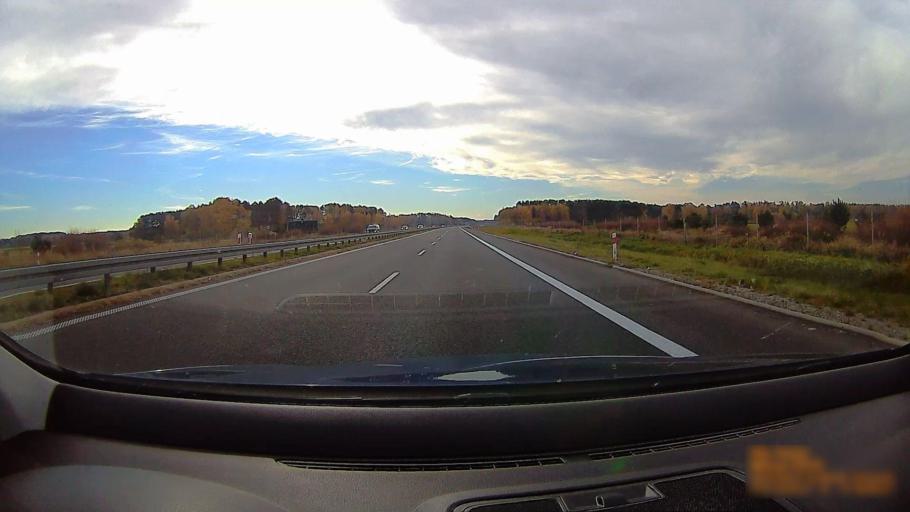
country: PL
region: Greater Poland Voivodeship
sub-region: Powiat ostrowski
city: Przygodzice
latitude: 51.5760
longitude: 17.8490
